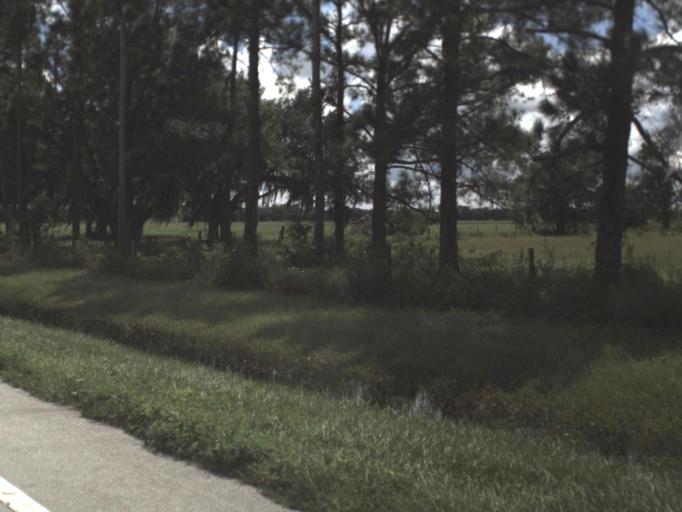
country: US
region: Florida
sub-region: DeSoto County
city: Arcadia
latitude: 27.2671
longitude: -81.9963
